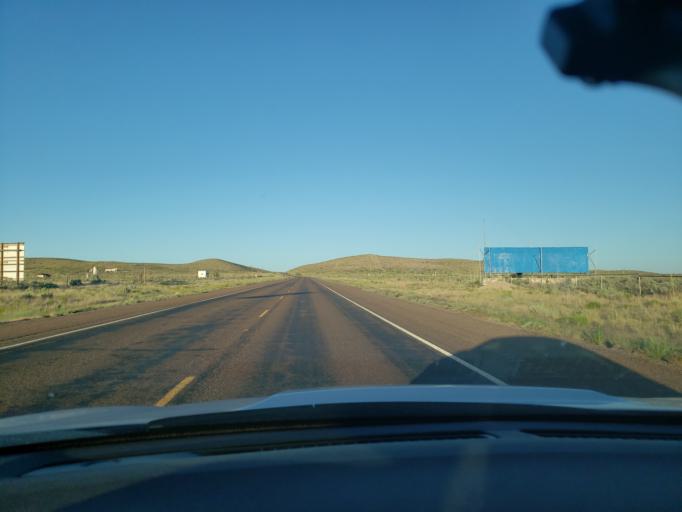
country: US
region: Texas
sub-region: El Paso County
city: Homestead Meadows South
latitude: 31.8267
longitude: -105.9065
